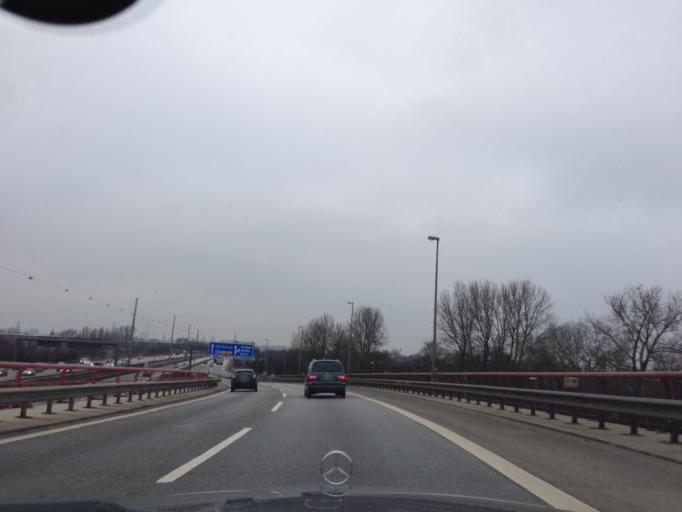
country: DE
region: Hamburg
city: Rothenburgsort
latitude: 53.5186
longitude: 10.0281
